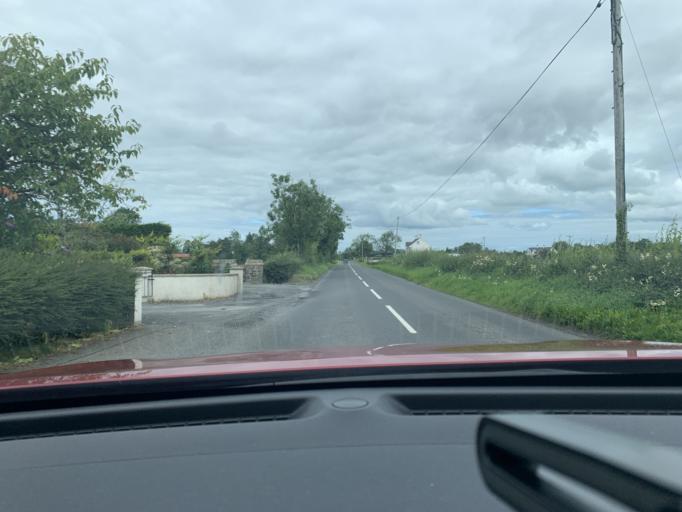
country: GB
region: Northern Ireland
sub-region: Fermanagh District
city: Enniskillen
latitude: 54.2700
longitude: -7.7049
